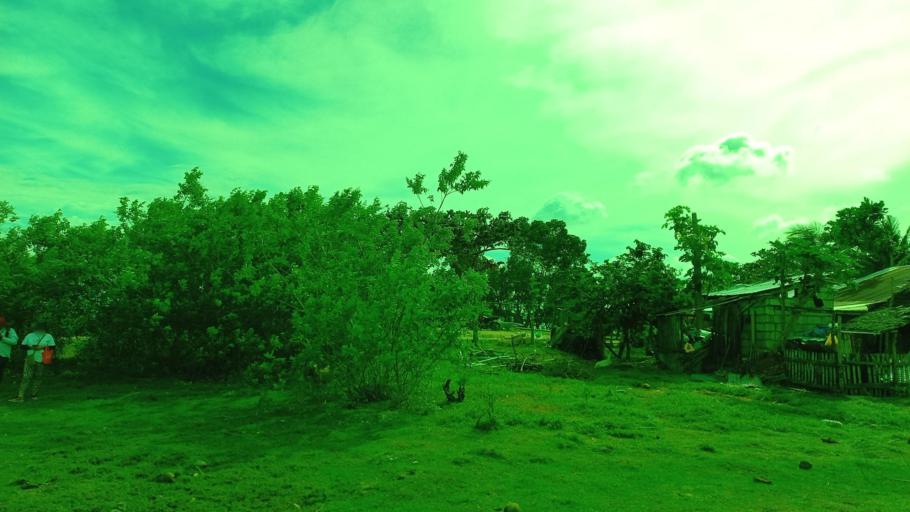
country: PH
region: Central Visayas
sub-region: Province of Siquijor
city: Lazi
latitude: 9.1250
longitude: 123.6481
